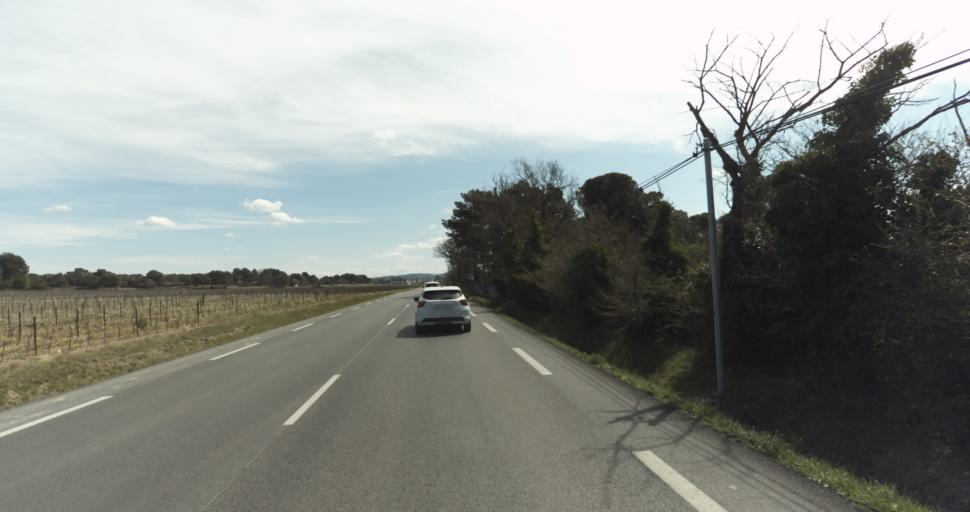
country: FR
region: Provence-Alpes-Cote d'Azur
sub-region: Departement des Bouches-du-Rhone
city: Eguilles
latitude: 43.5914
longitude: 5.3607
